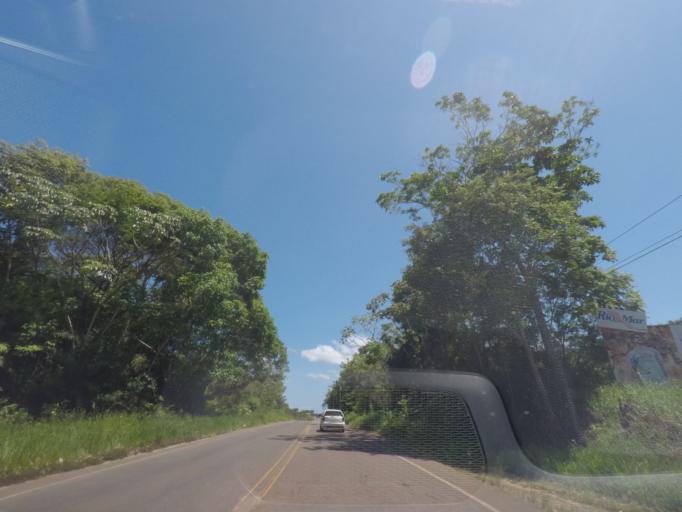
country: BR
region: Bahia
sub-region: Valenca
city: Valenca
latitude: -13.3423
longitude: -39.0649
